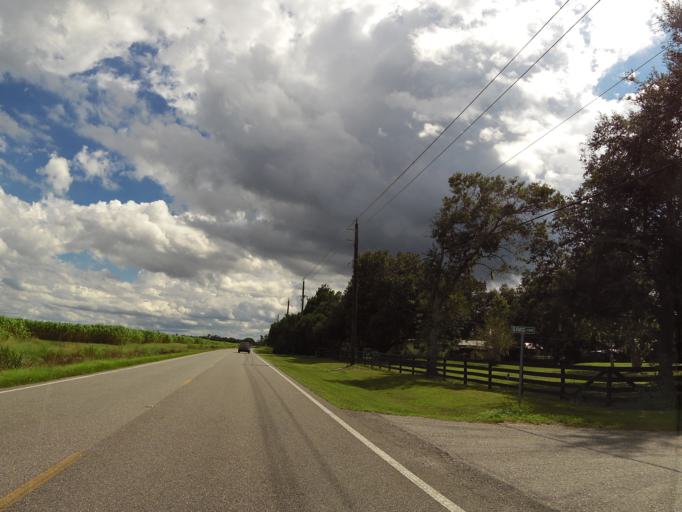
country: US
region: Florida
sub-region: Saint Johns County
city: Saint Augustine South
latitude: 29.8080
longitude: -81.4845
